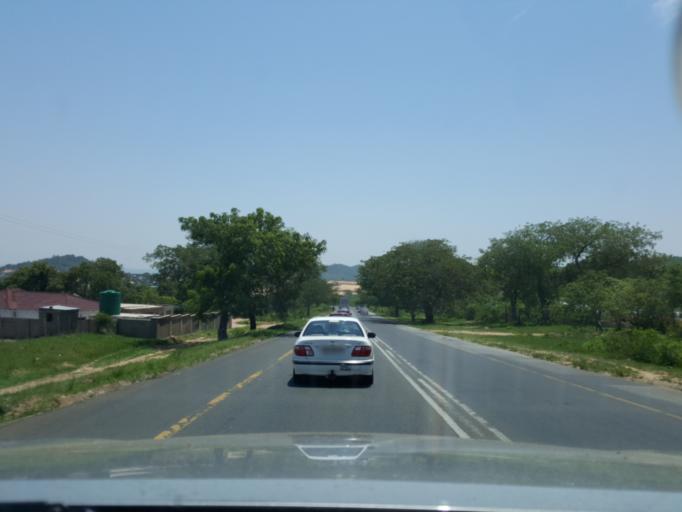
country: ZA
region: Limpopo
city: Thulamahashi
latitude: -24.8278
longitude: 31.0828
